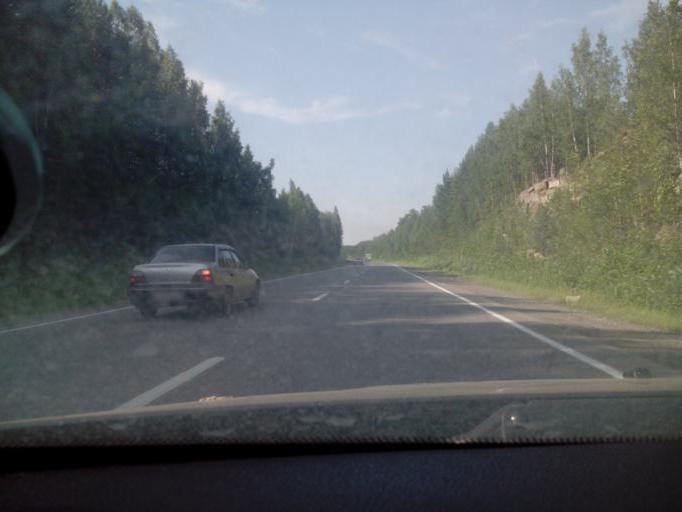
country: RU
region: Sverdlovsk
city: Verkh-Neyvinskiy
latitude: 57.2695
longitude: 60.2941
